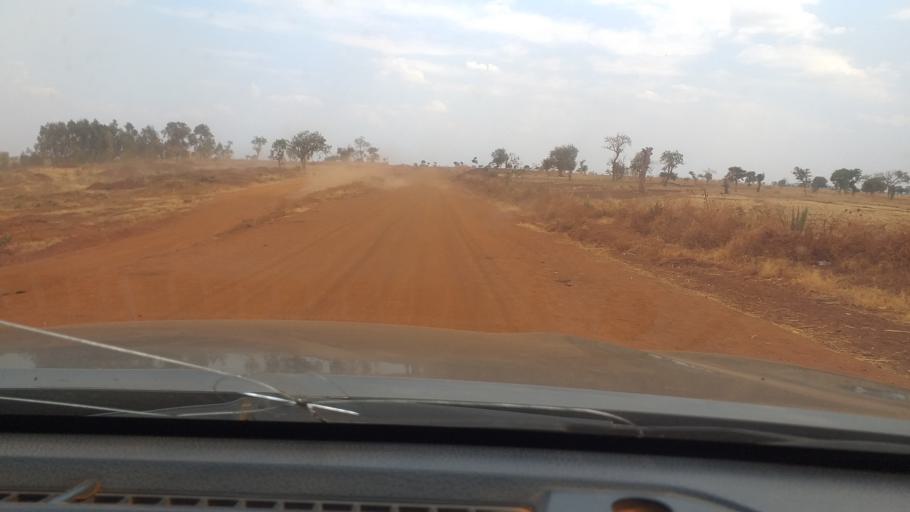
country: ET
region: Binshangul Gumuz
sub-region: Asosa
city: Asosa
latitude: 10.0652
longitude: 34.6819
